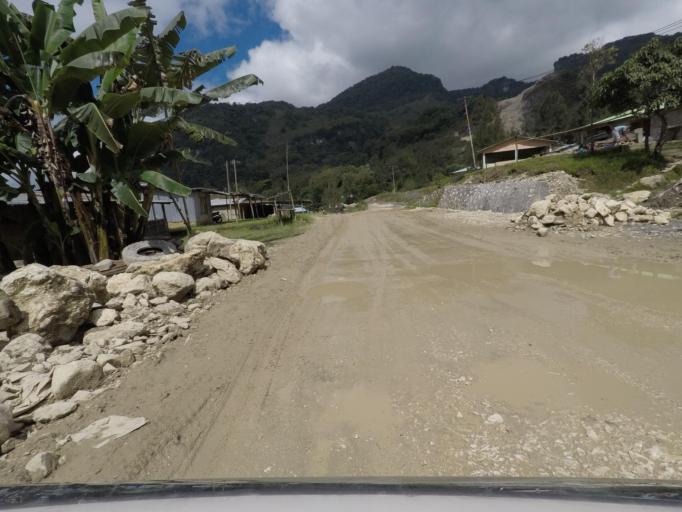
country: TL
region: Baucau
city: Venilale
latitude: -8.7088
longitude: 126.3644
